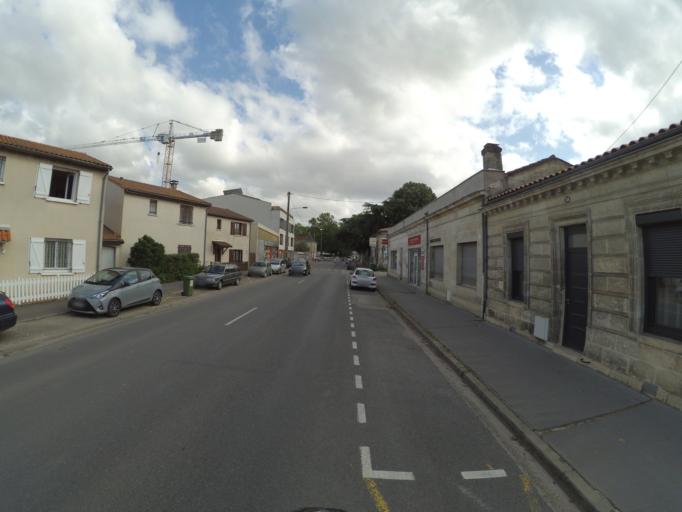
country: FR
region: Aquitaine
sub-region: Departement de la Gironde
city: Lormont
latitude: 44.8768
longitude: -0.5533
